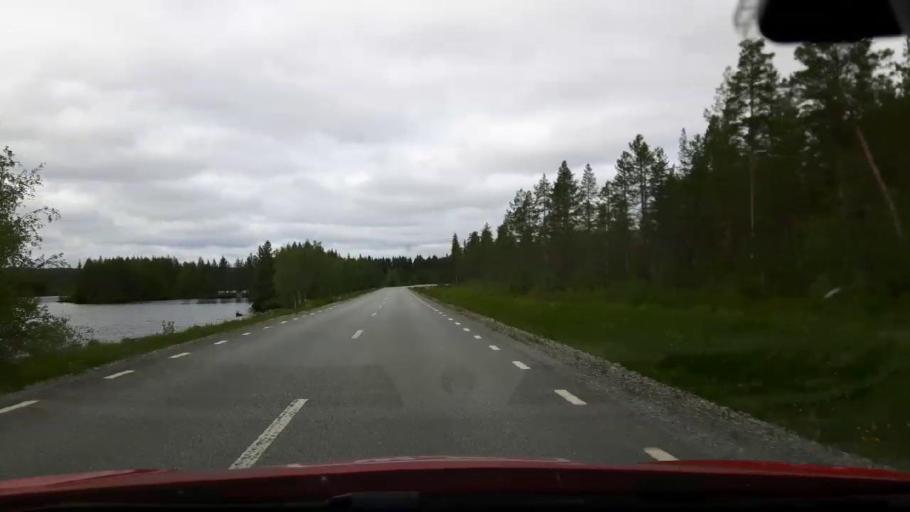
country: SE
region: Jaemtland
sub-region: OEstersunds Kommun
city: Lit
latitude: 63.6815
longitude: 14.6774
